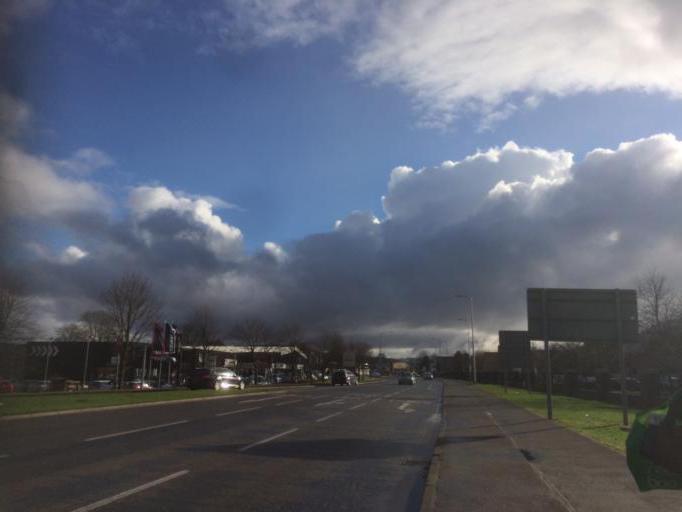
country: GB
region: Scotland
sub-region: Perth and Kinross
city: Luncarty
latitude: 56.4185
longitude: -3.4644
